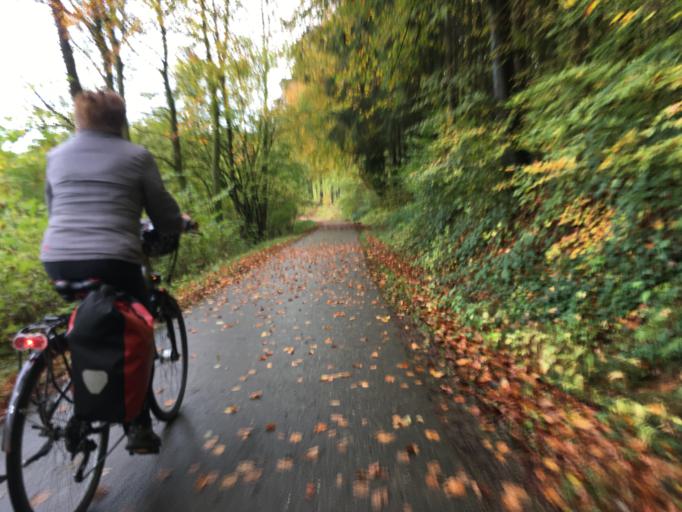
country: DE
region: Baden-Wuerttemberg
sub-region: Regierungsbezirk Stuttgart
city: Mockmuhl
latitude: 49.3107
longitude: 9.3836
